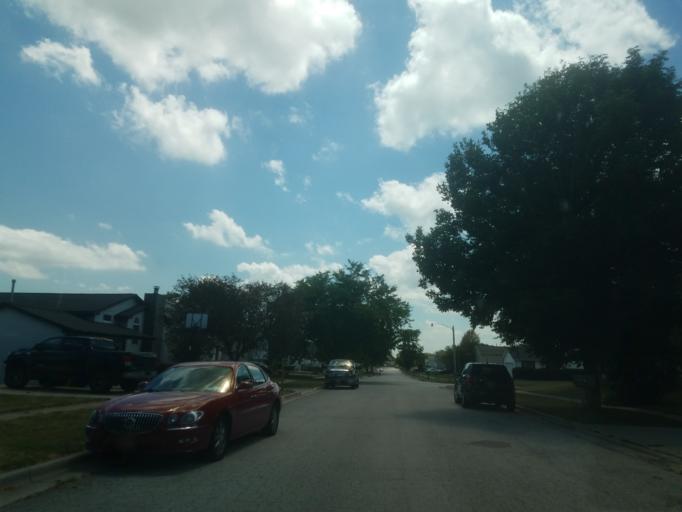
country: US
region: Illinois
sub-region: McLean County
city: Bloomington
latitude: 40.4445
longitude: -89.0295
